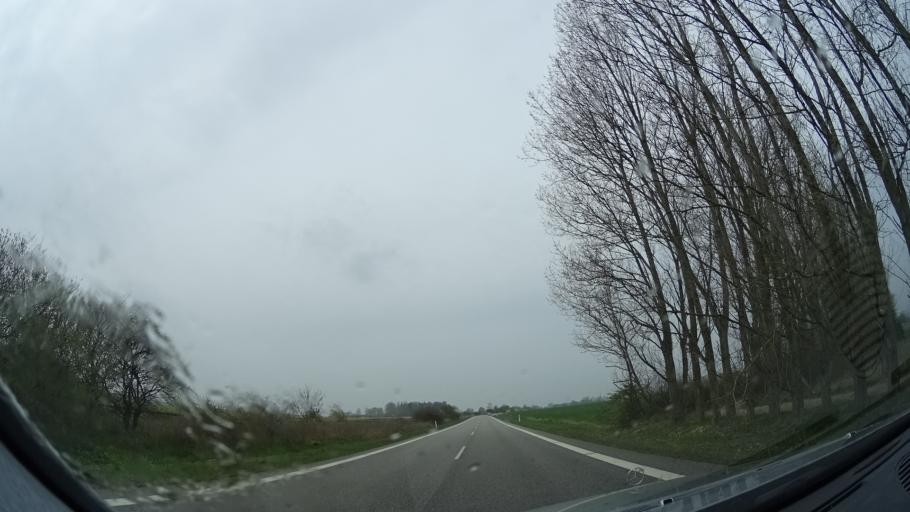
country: DK
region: Zealand
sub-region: Holbaek Kommune
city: Holbaek
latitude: 55.7166
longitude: 11.6499
